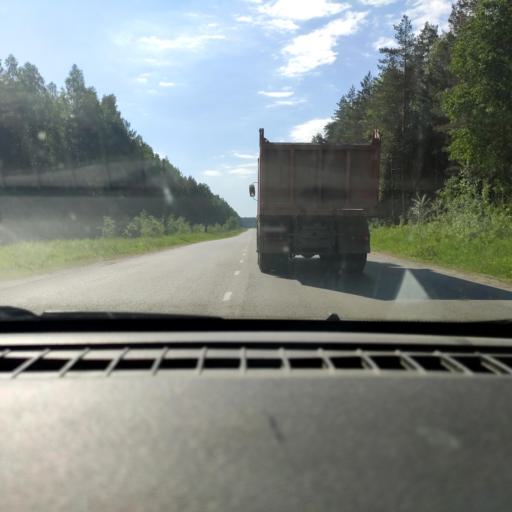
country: RU
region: Perm
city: Overyata
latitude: 58.0164
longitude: 55.8618
